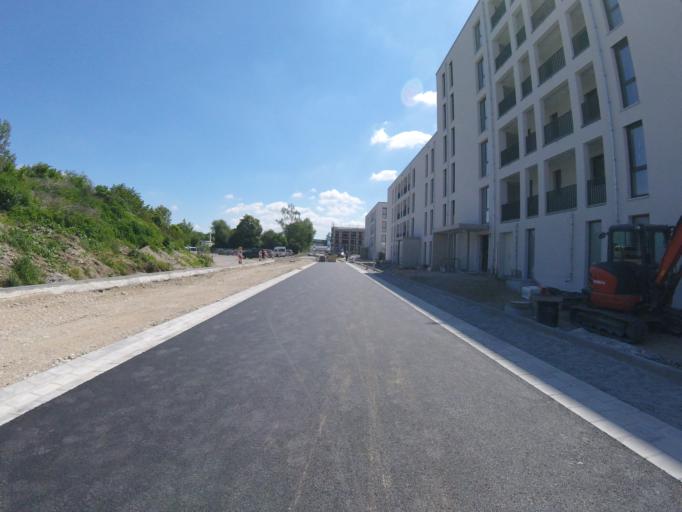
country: DE
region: Bavaria
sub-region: Upper Bavaria
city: Unterhaching
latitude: 48.1024
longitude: 11.6222
